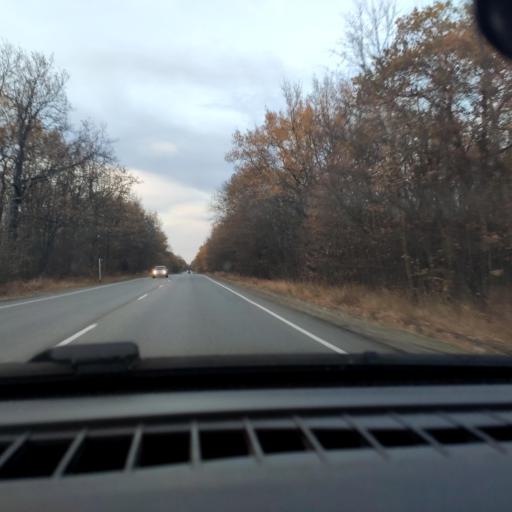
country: RU
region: Voronezj
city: Devitsa
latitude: 51.6234
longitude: 38.9877
